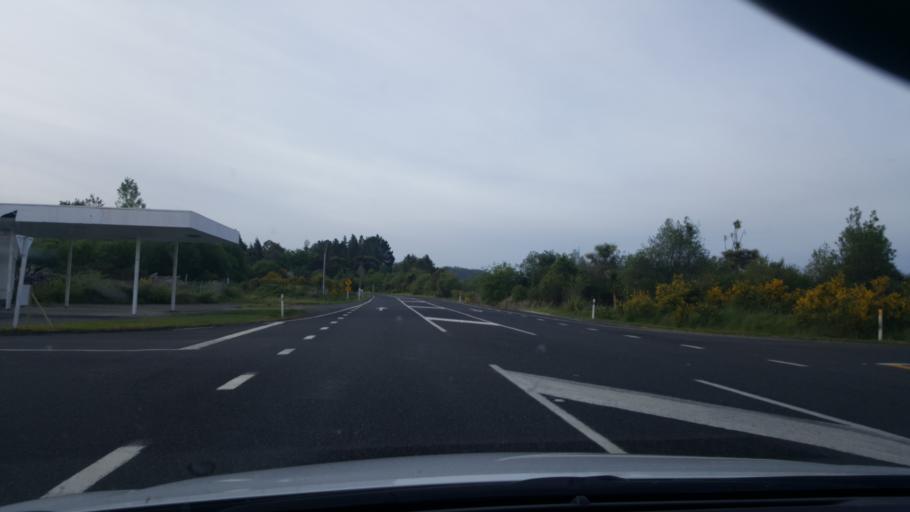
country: NZ
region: Waikato
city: Turangi
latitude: -38.9630
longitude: 175.7655
